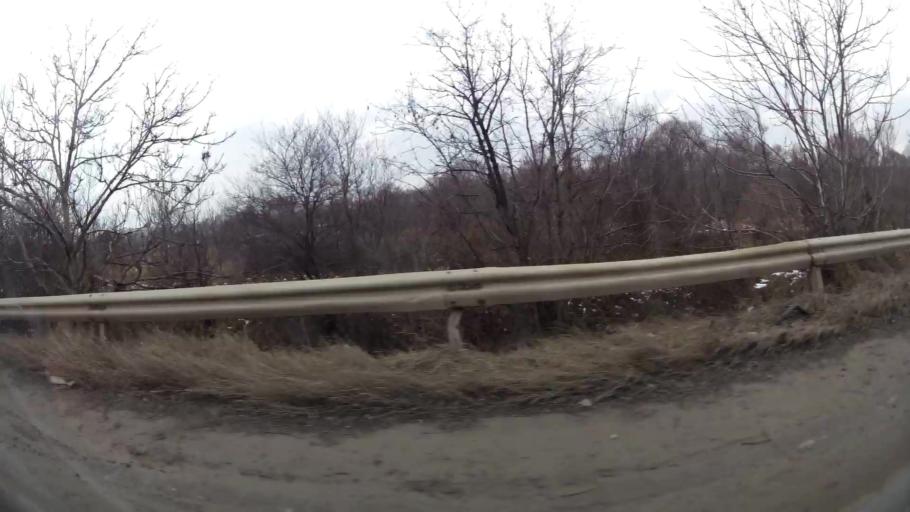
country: BG
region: Sofiya
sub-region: Obshtina Bozhurishte
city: Bozhurishte
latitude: 42.7006
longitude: 23.2303
